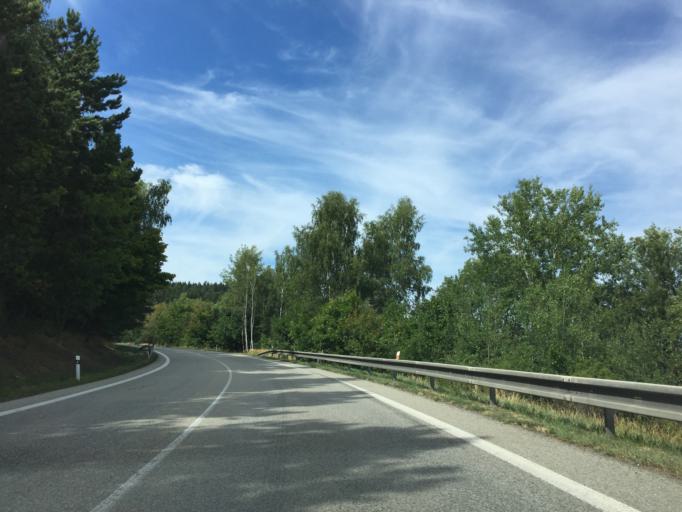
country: CZ
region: Central Bohemia
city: Votice
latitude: 49.5785
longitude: 14.6623
